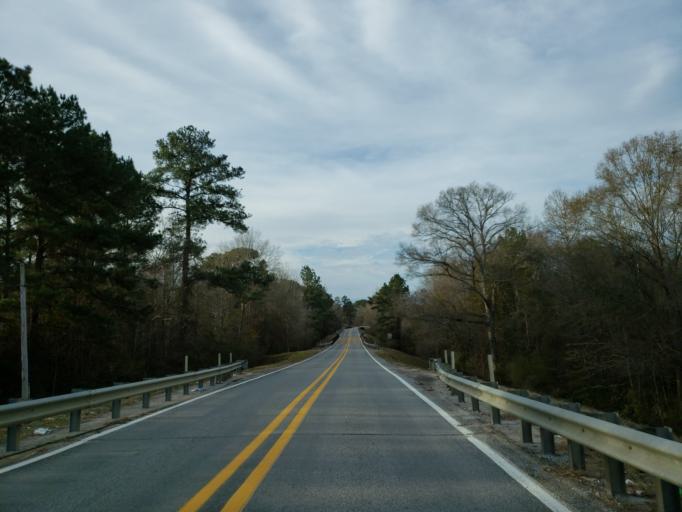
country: US
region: Mississippi
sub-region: Wayne County
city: Waynesboro
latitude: 31.8537
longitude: -88.6951
